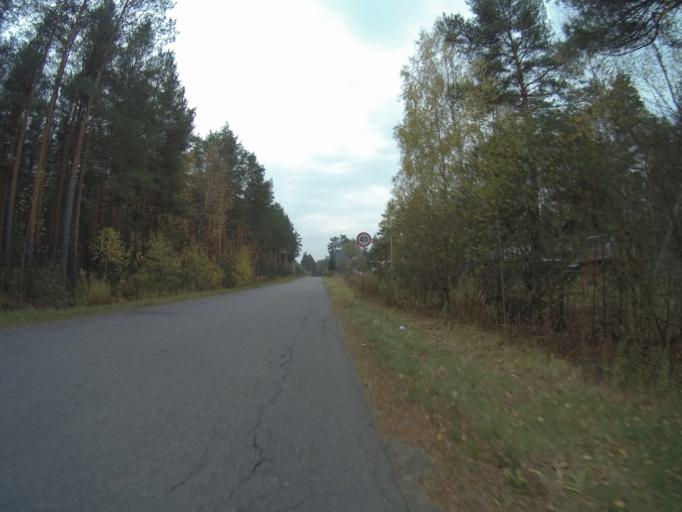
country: RU
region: Vladimir
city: Kommunar
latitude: 56.1407
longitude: 40.4931
